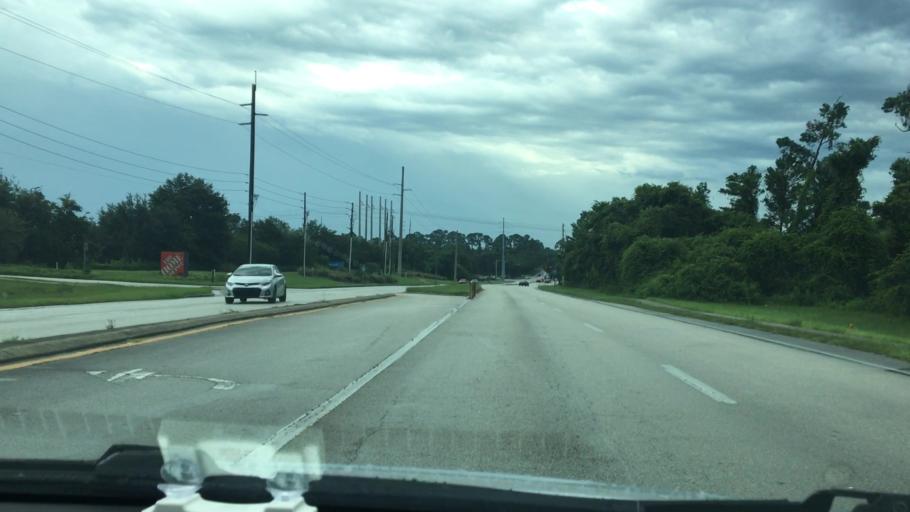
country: US
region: Florida
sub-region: Volusia County
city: Deltona
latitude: 28.9152
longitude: -81.2818
